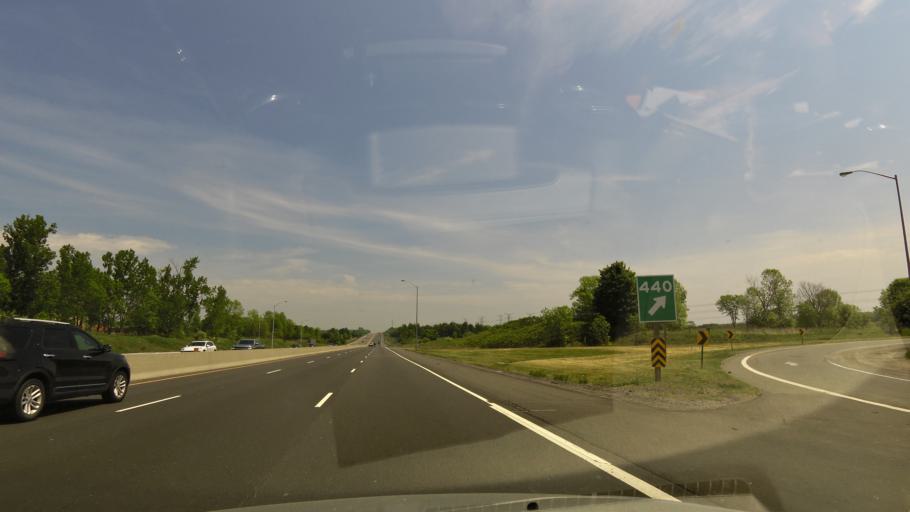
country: CA
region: Ontario
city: Oshawa
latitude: 43.9107
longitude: -78.5850
